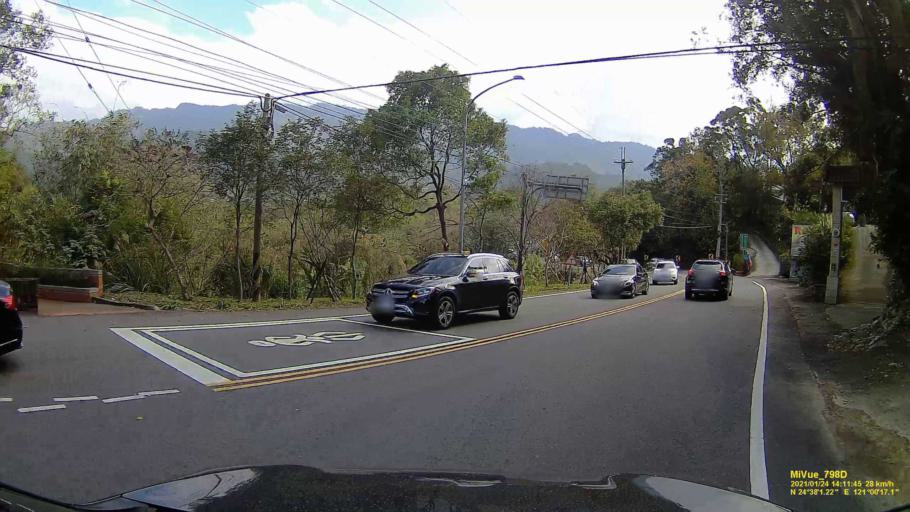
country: TW
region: Taiwan
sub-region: Hsinchu
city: Hsinchu
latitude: 24.6336
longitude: 121.0048
